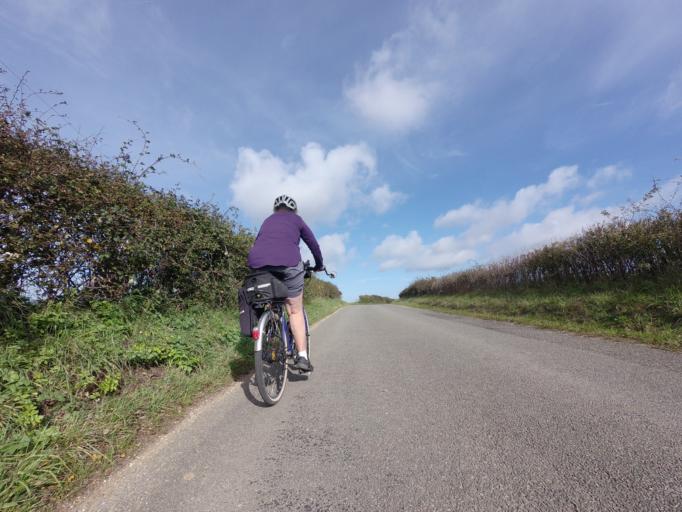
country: GB
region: England
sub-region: Norfolk
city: Wells-next-the-Sea
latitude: 52.9297
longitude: 0.7238
